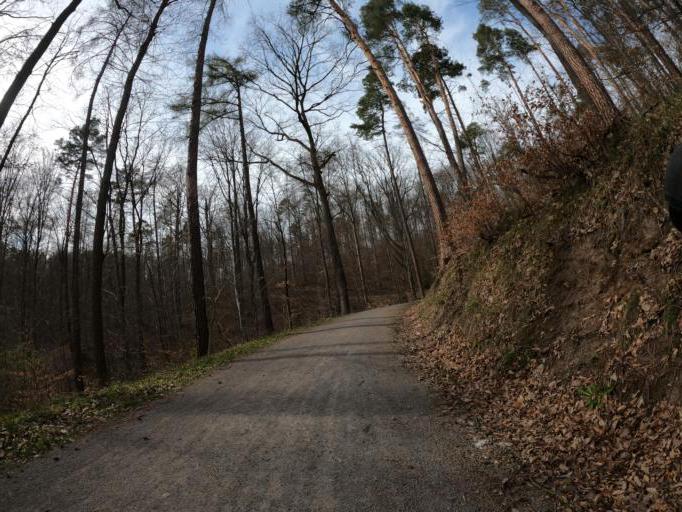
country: DE
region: Baden-Wuerttemberg
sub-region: Regierungsbezirk Stuttgart
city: Stuttgart-Ost
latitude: 48.7584
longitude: 9.2043
